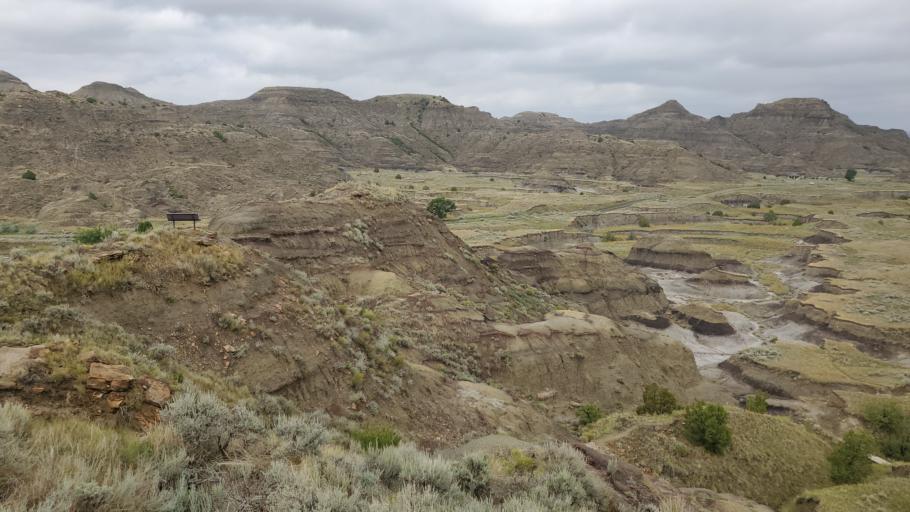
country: US
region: Montana
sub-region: Dawson County
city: Glendive
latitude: 47.0762
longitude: -104.6923
